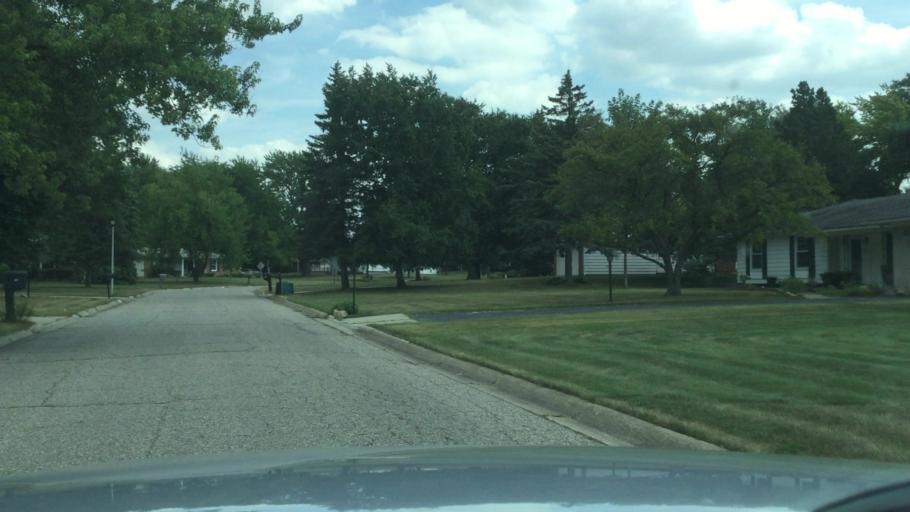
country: US
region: Michigan
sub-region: Genesee County
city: Grand Blanc
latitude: 42.9500
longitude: -83.6735
